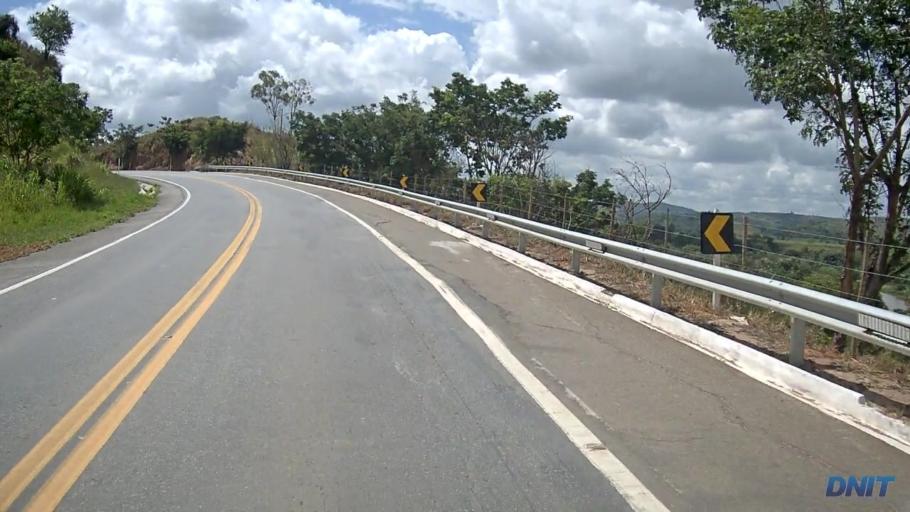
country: BR
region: Minas Gerais
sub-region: Governador Valadares
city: Governador Valadares
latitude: -18.9244
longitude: -42.0209
